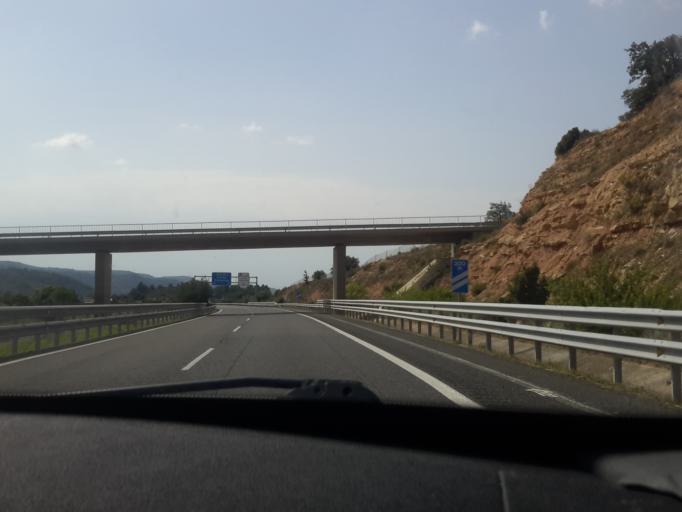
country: ES
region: Catalonia
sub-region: Provincia de Lleida
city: Vinaixa
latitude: 41.4265
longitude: 0.9446
